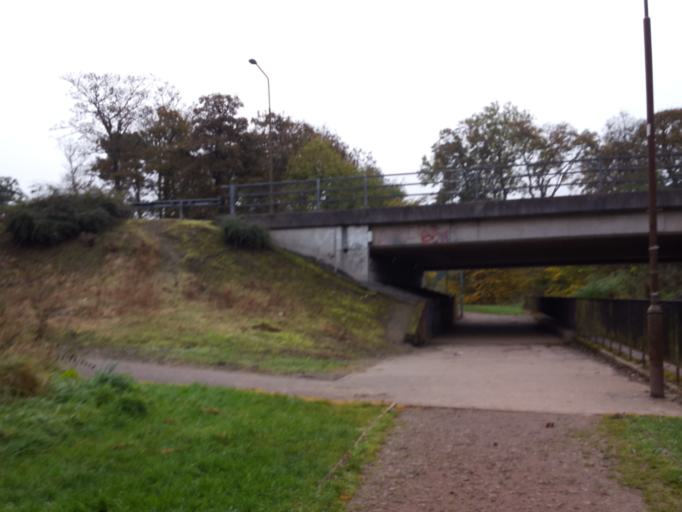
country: GB
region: Scotland
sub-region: West Lothian
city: Livingston
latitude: 55.8972
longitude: -3.5509
